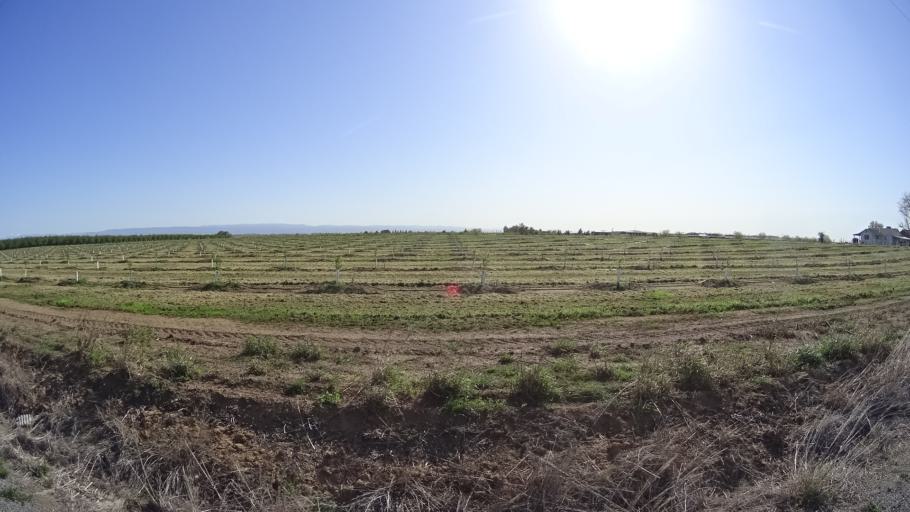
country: US
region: California
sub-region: Glenn County
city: Hamilton City
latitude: 39.7701
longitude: -122.0666
